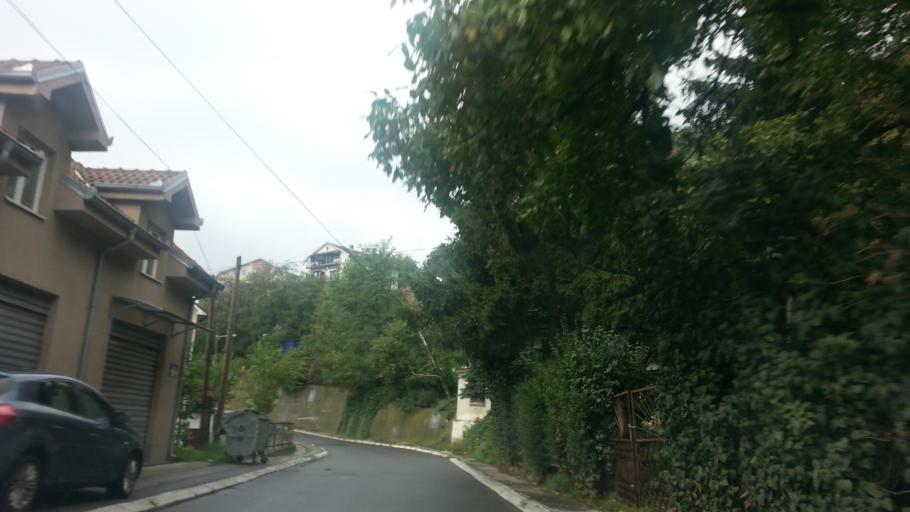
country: RS
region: Central Serbia
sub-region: Belgrade
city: Rakovica
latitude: 44.7493
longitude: 20.4431
